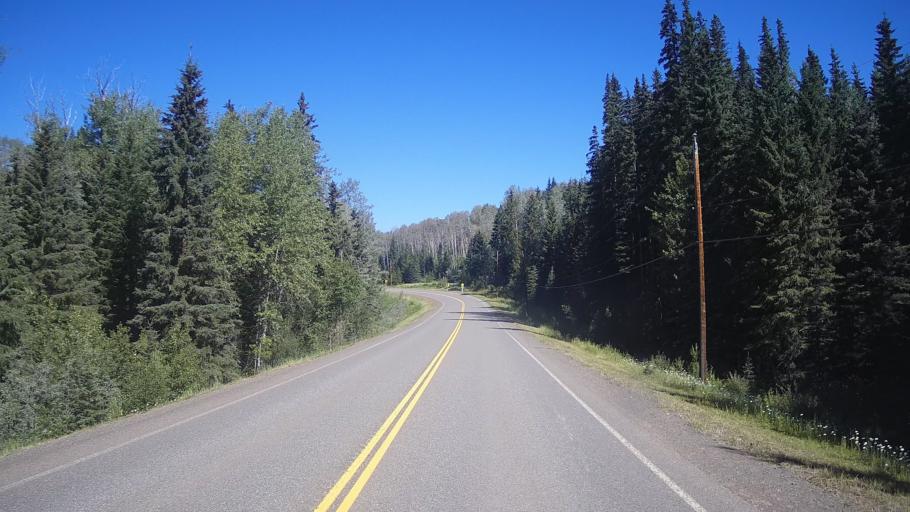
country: CA
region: British Columbia
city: Kamloops
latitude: 51.5028
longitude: -120.6008
